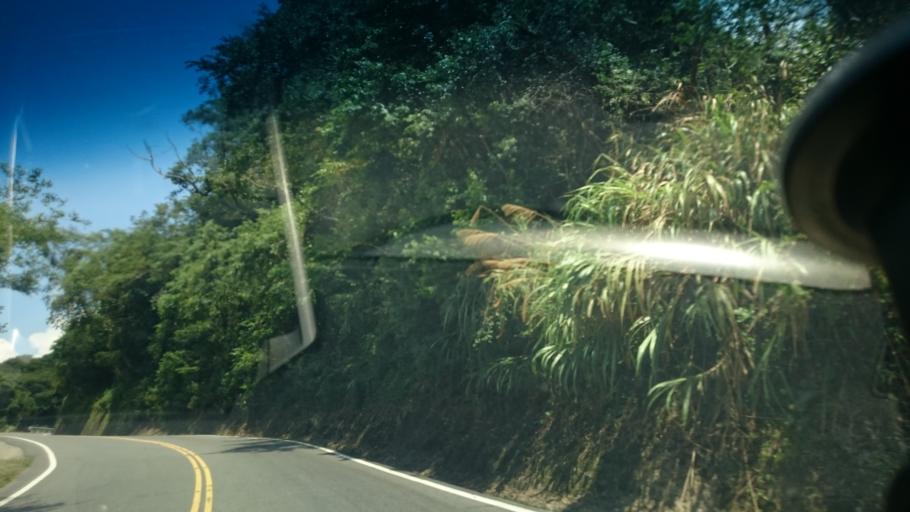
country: TW
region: Taiwan
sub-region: Nantou
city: Puli
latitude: 24.0143
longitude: 121.1218
